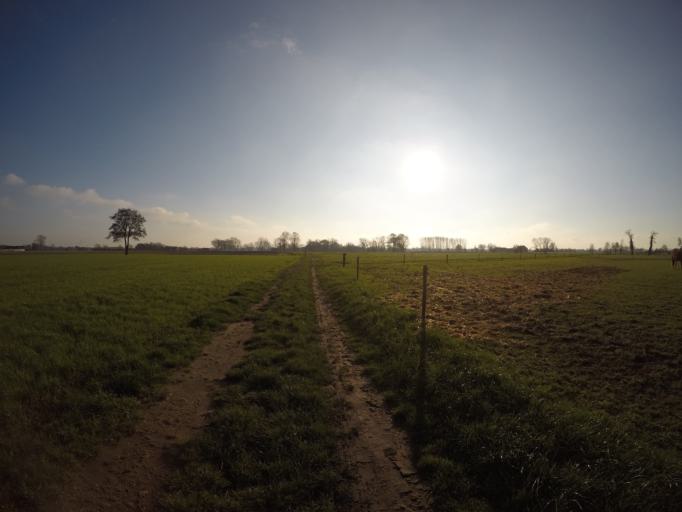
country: BE
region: Flanders
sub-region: Provincie West-Vlaanderen
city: Lichtervelde
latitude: 51.0630
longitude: 3.1926
